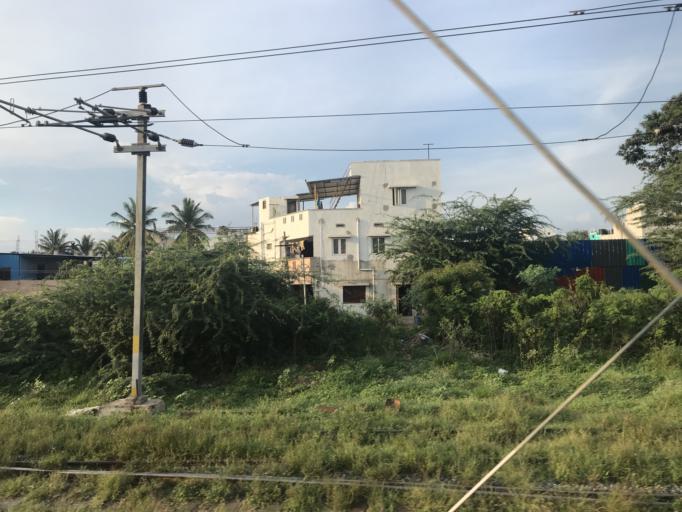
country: IN
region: Tamil Nadu
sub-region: Coimbatore
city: Coimbatore
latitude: 11.0343
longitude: 76.9921
